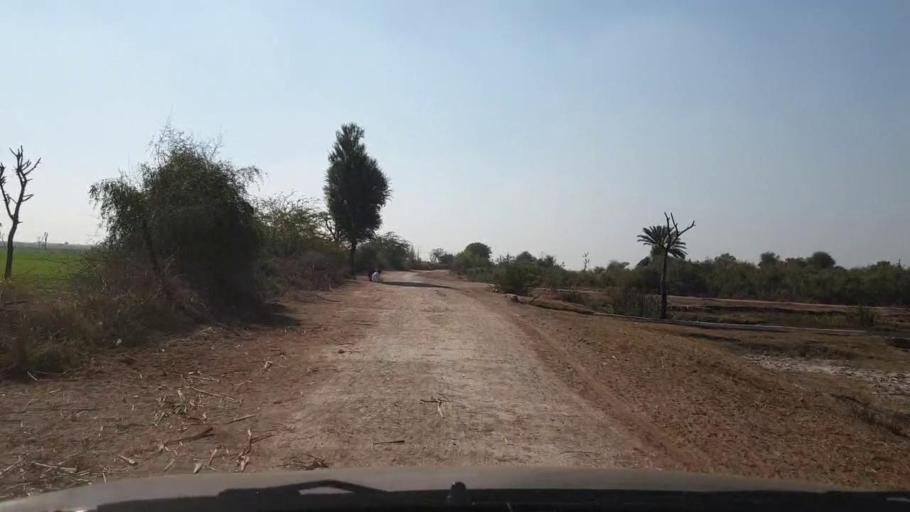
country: PK
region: Sindh
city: Jhol
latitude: 25.9227
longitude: 68.7945
